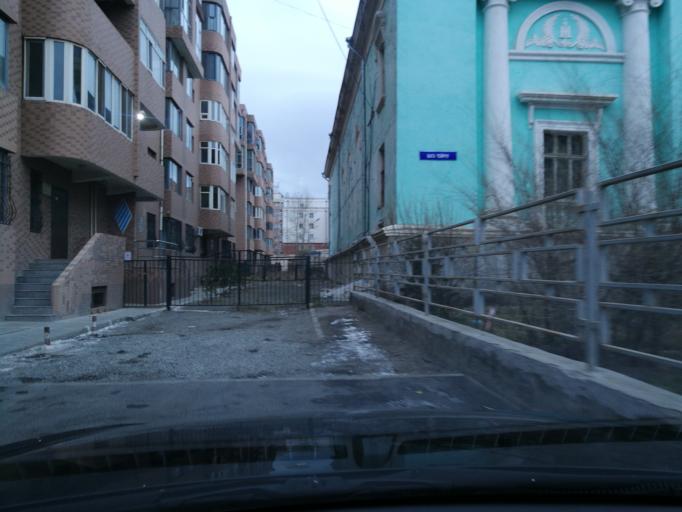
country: MN
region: Ulaanbaatar
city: Ulaanbaatar
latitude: 47.9264
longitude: 106.9157
